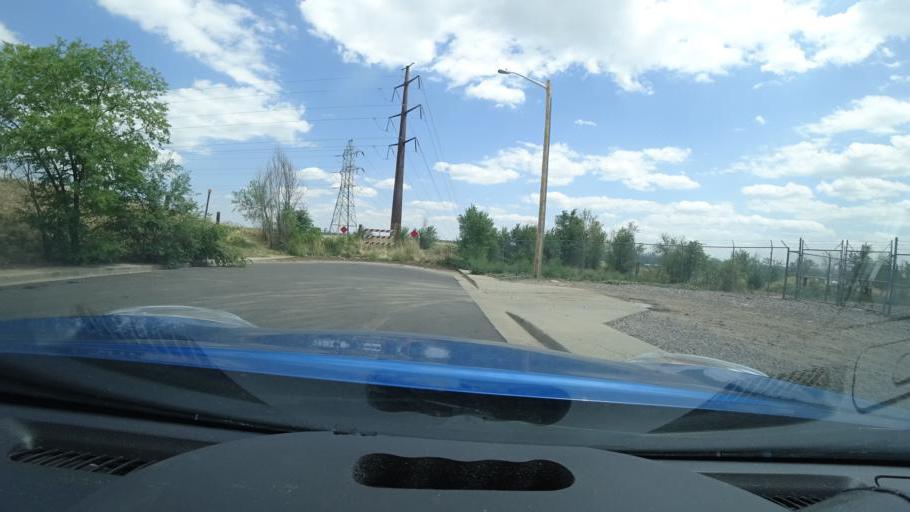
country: US
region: Colorado
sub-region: Arapahoe County
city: Englewood
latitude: 39.6813
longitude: -105.0070
